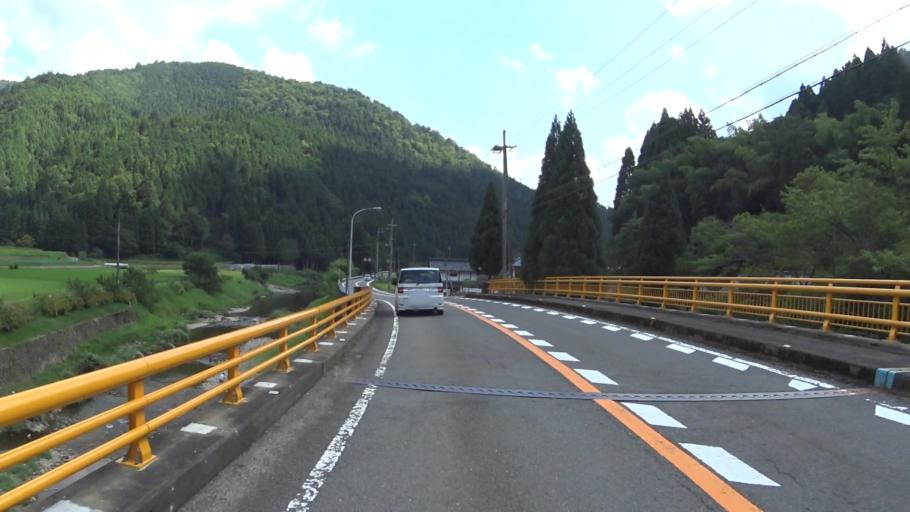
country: JP
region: Kyoto
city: Maizuru
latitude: 35.2942
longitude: 135.5570
